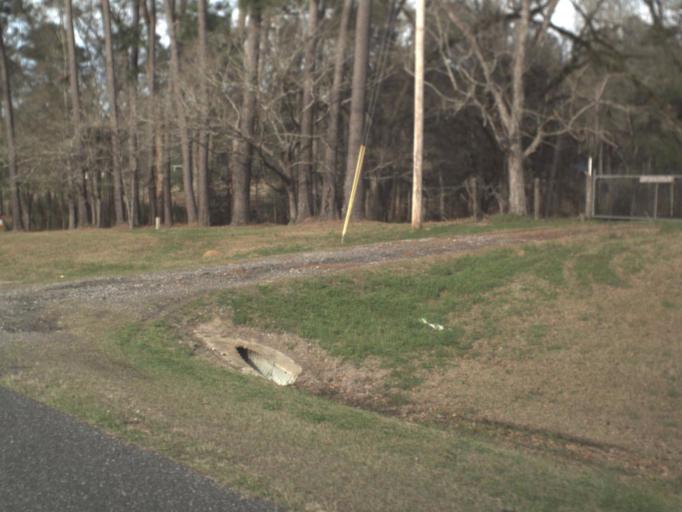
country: US
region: Florida
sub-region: Jefferson County
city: Monticello
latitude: 30.6091
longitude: -83.8720
